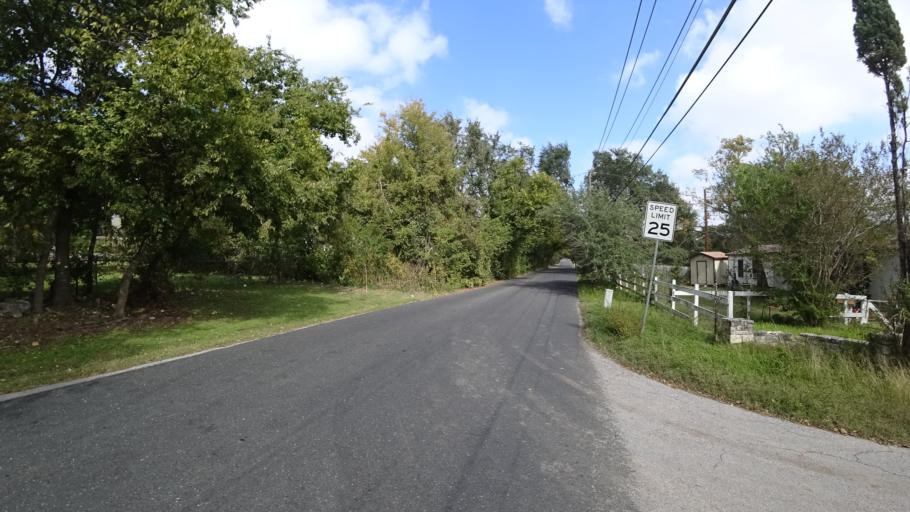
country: US
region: Texas
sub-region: Travis County
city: Shady Hollow
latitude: 30.1987
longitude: -97.8300
